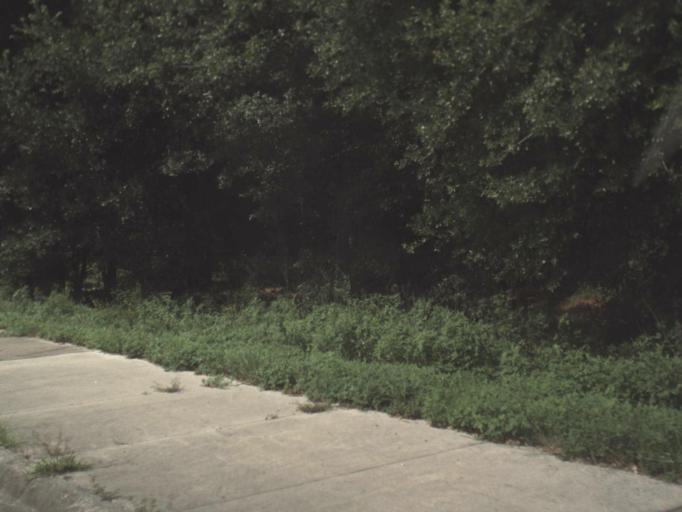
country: US
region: Florida
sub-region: Citrus County
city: Inverness Highlands South
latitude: 28.8024
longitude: -82.3098
